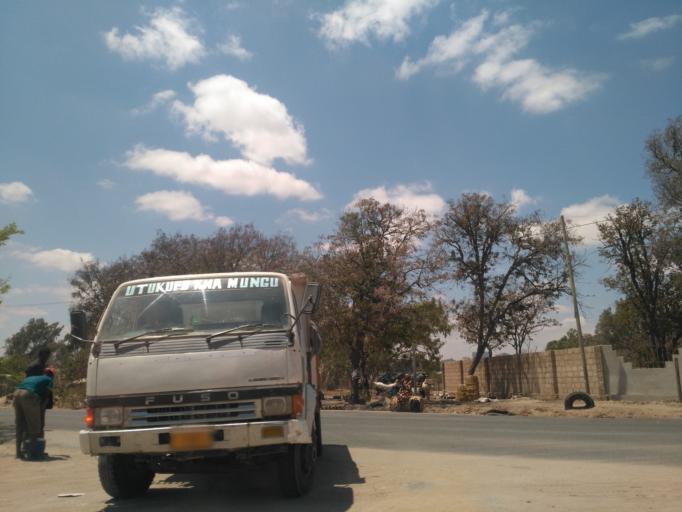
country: TZ
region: Dodoma
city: Dodoma
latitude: -6.1744
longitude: 35.7530
